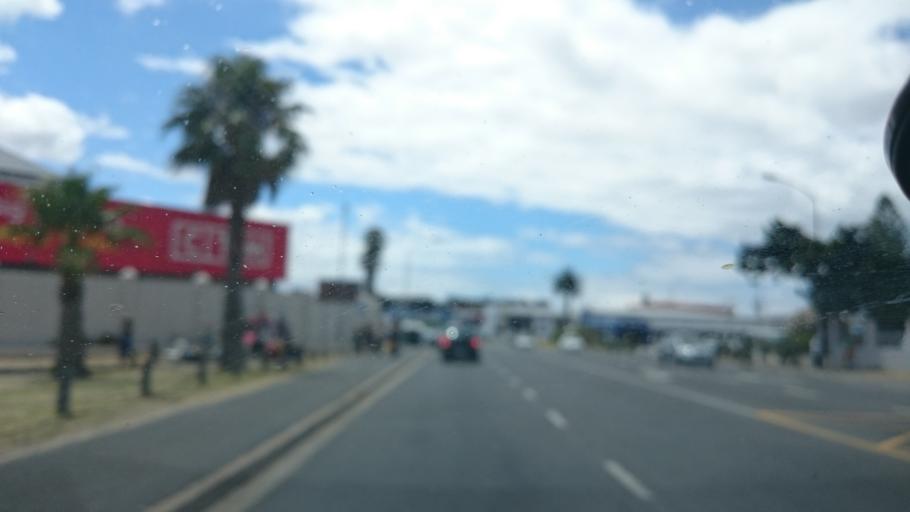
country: ZA
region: Western Cape
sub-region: City of Cape Town
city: Bergvliet
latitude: -34.0658
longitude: 18.4572
